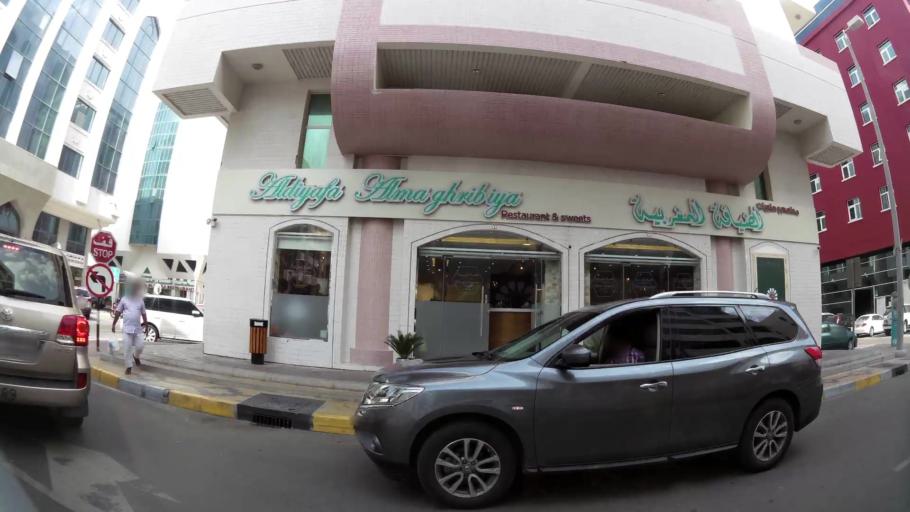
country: AE
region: Abu Dhabi
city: Abu Dhabi
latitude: 24.4783
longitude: 54.3577
